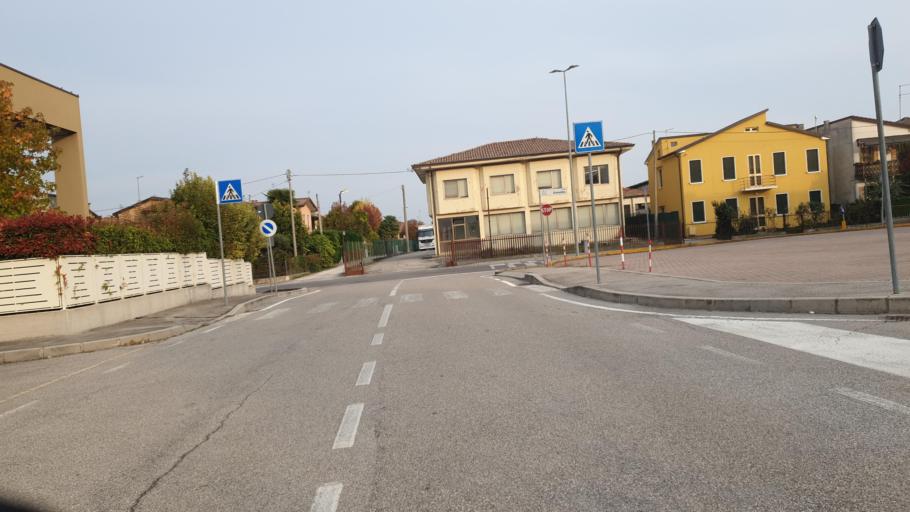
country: IT
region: Veneto
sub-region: Provincia di Venezia
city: Tombelle
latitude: 45.3949
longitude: 11.9808
